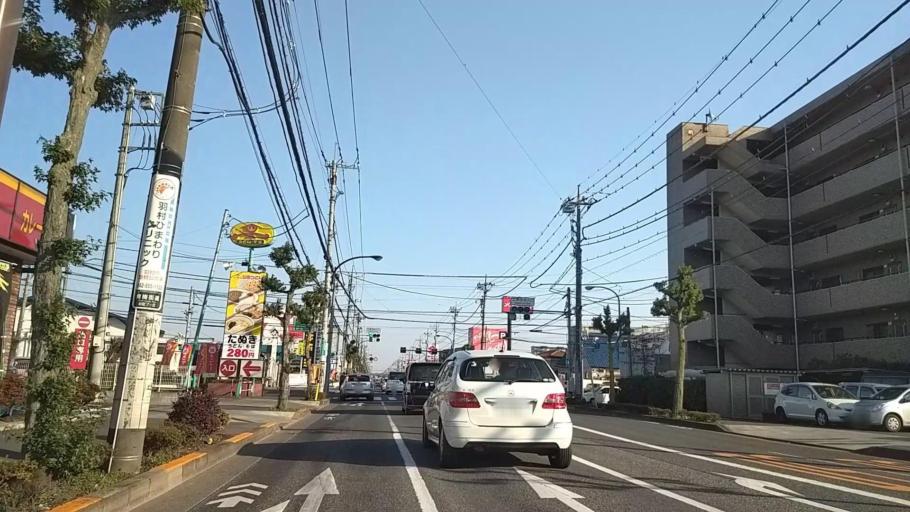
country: JP
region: Tokyo
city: Fussa
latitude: 35.7834
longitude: 139.3169
